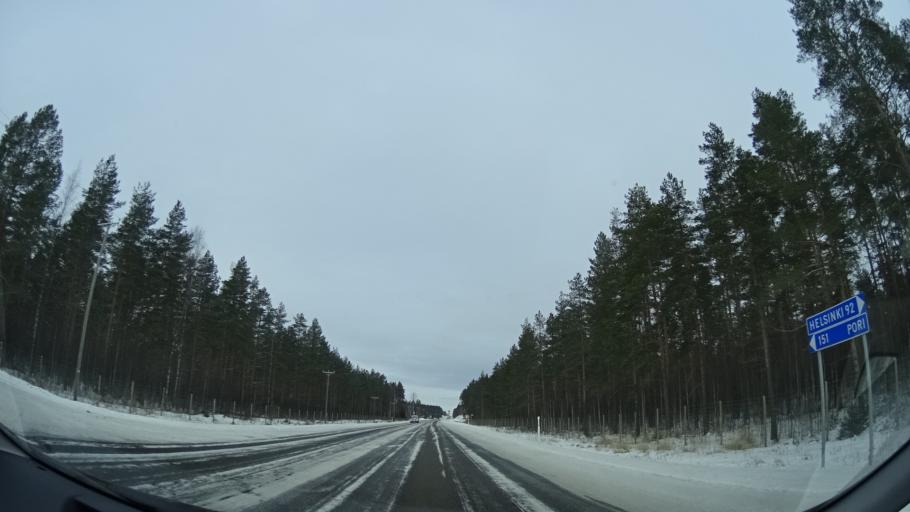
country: FI
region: Uusimaa
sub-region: Helsinki
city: Kaerkoelae
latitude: 60.6462
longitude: 23.8734
